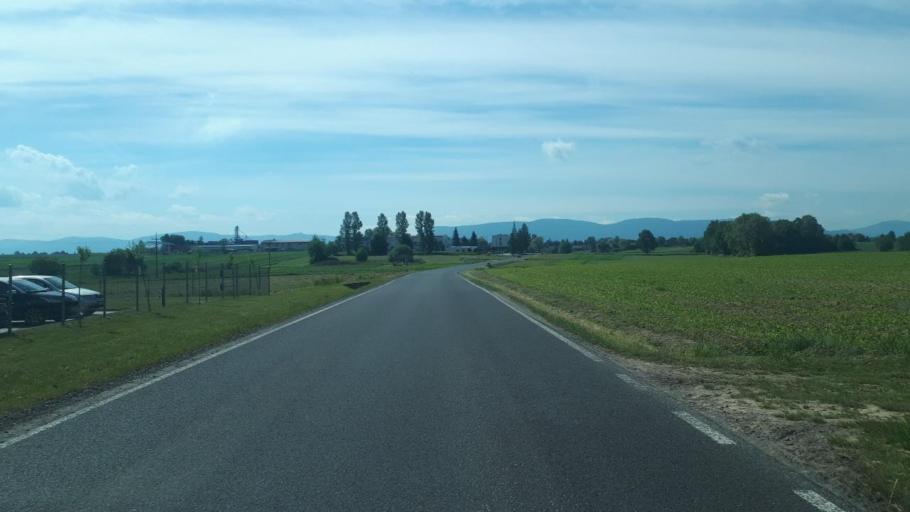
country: PL
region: Silesian Voivodeship
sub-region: Powiat bielski
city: Wilamowice
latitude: 49.9292
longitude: 19.1488
